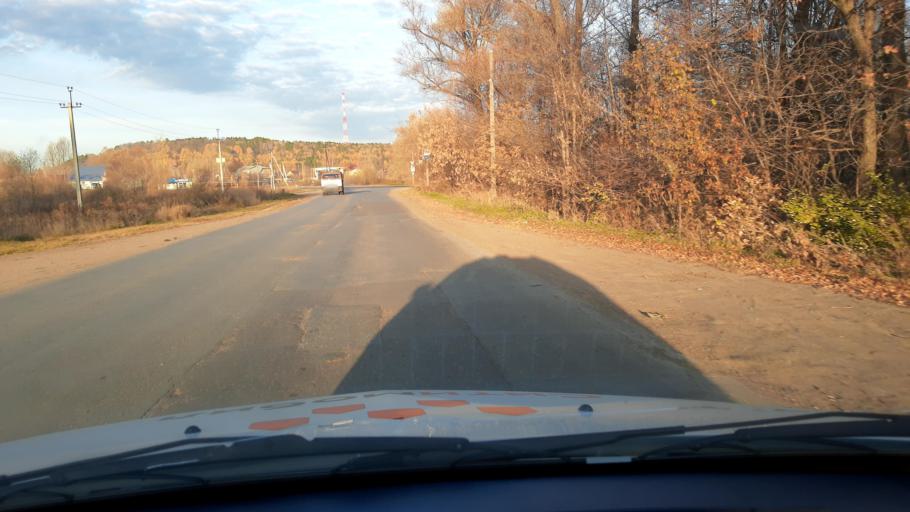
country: RU
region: Bashkortostan
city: Ufa
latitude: 54.8106
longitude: 56.1632
